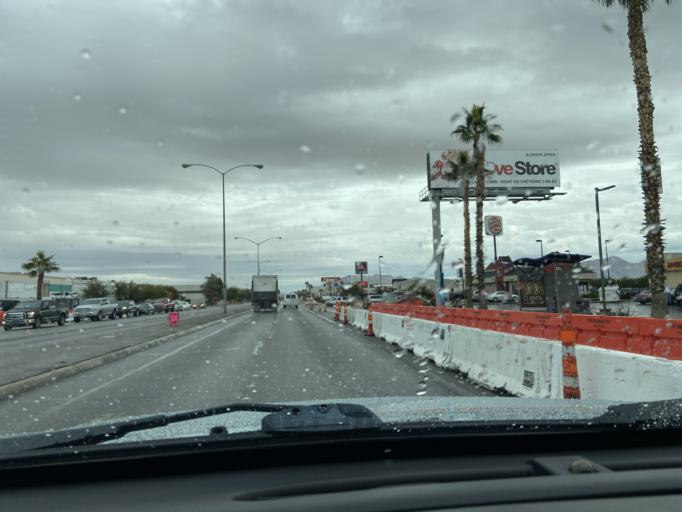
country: US
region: Nevada
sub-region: Clark County
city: Sunrise Manor
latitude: 36.2402
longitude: -115.0969
